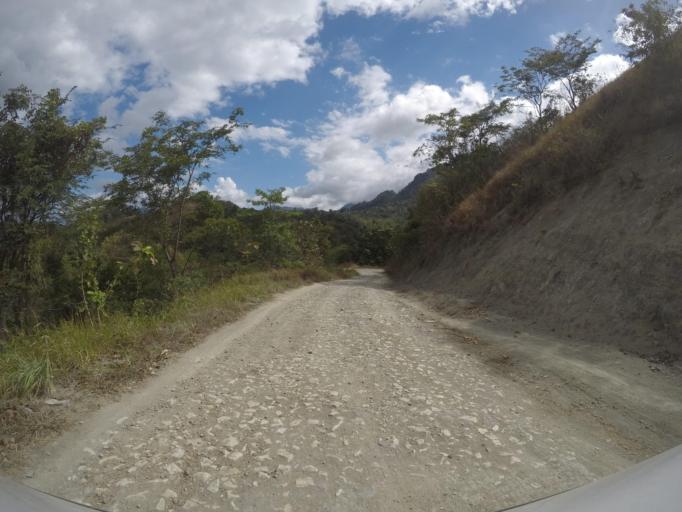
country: TL
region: Baucau
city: Baucau
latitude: -8.6187
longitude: 126.6613
